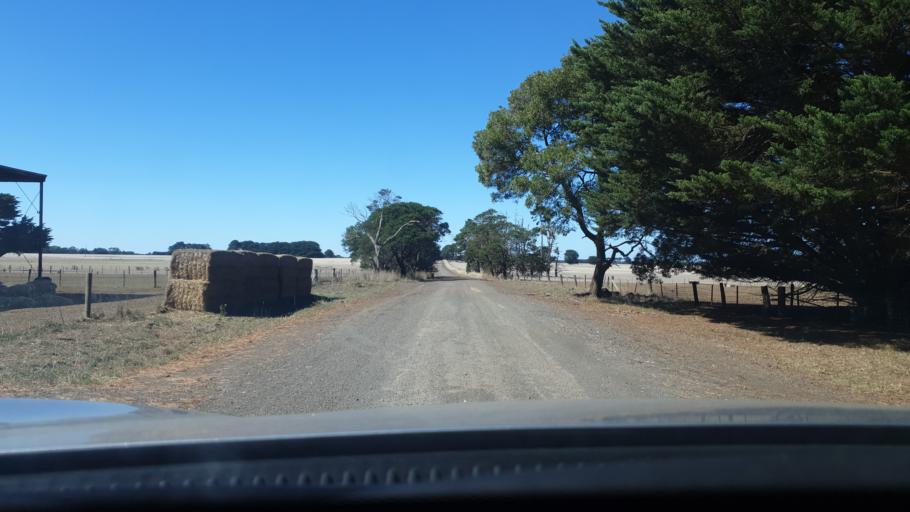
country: AU
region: Victoria
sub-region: Warrnambool
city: Warrnambool
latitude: -38.1650
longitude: 142.3765
